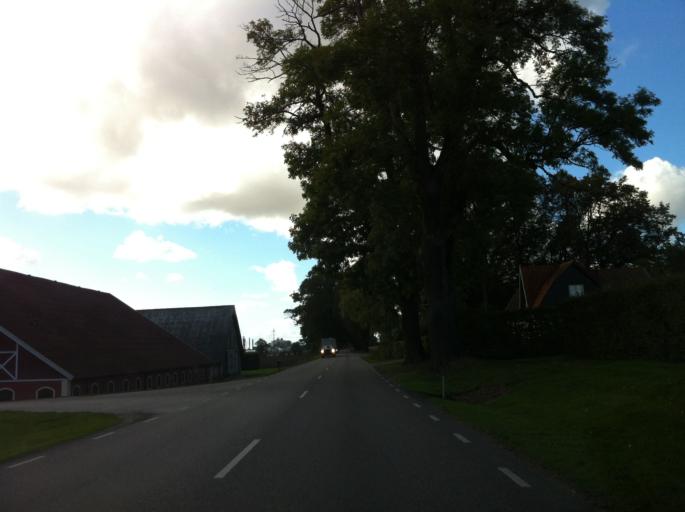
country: SE
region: Skane
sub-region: Eslovs Kommun
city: Eslov
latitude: 55.7795
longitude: 13.2941
